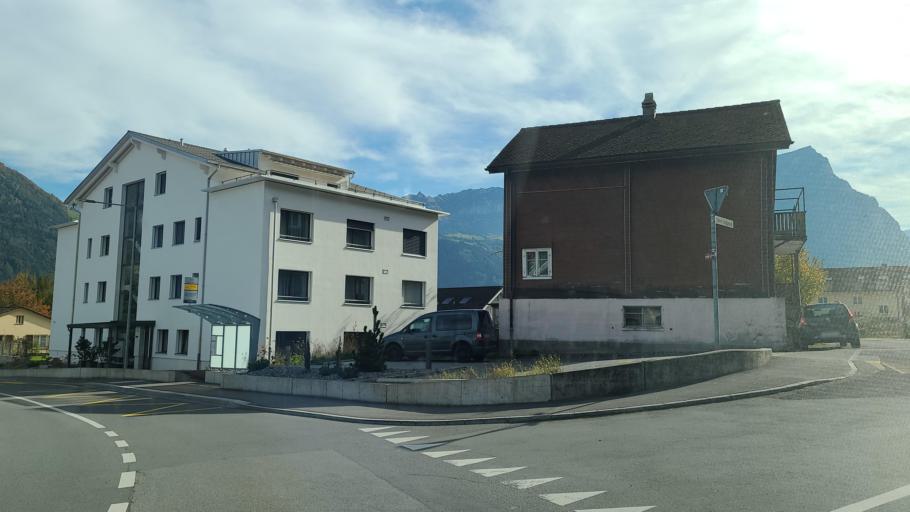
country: CH
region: Uri
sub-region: Uri
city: Seedorf
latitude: 46.8809
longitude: 8.6133
